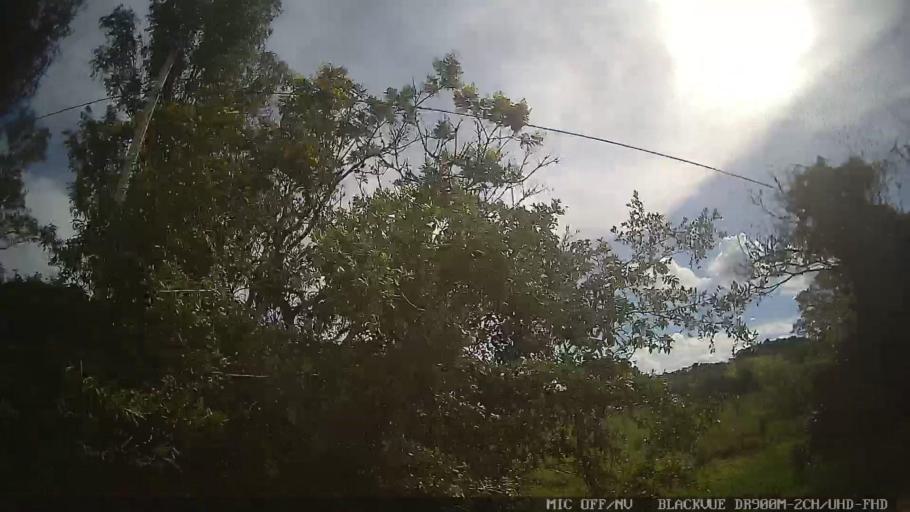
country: BR
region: Sao Paulo
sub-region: Conchas
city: Conchas
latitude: -23.0550
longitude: -47.9829
